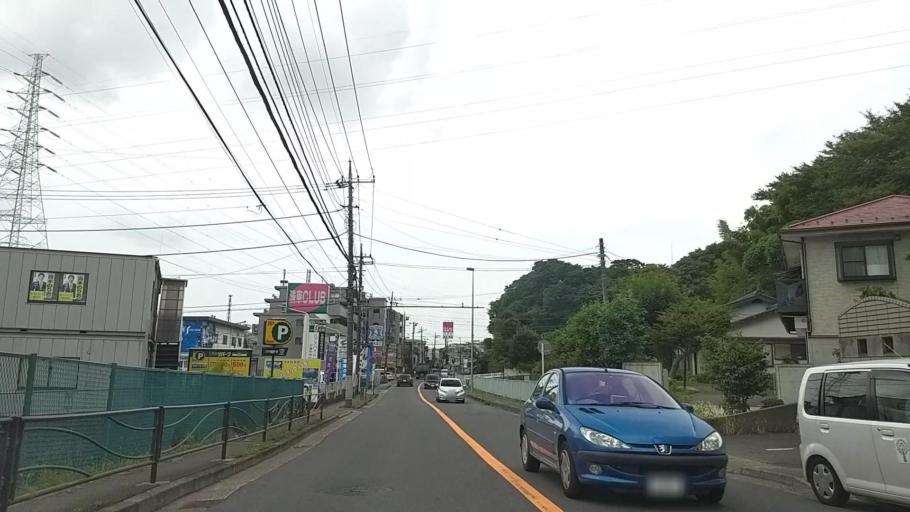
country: JP
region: Kanagawa
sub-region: Kawasaki-shi
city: Kawasaki
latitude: 35.5681
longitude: 139.6153
